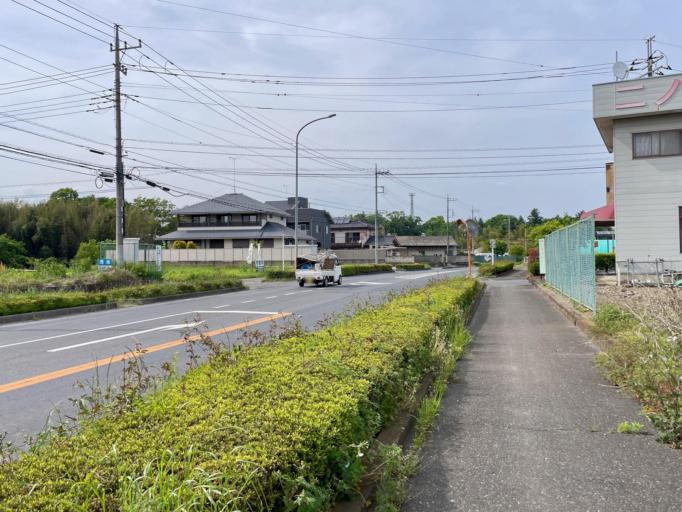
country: JP
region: Tochigi
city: Mibu
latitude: 36.3932
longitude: 139.8032
